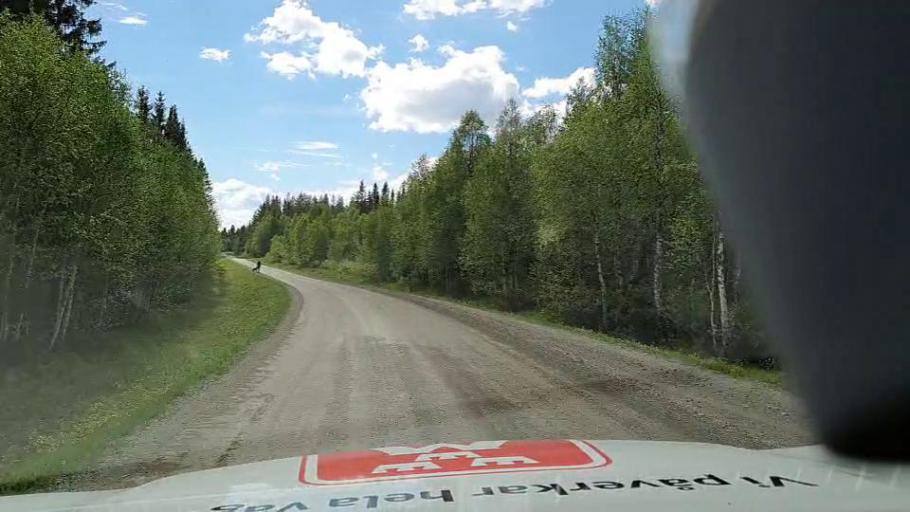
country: SE
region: Vaesterbotten
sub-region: Vilhelmina Kommun
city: Sjoberg
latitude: 64.5498
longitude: 15.7968
